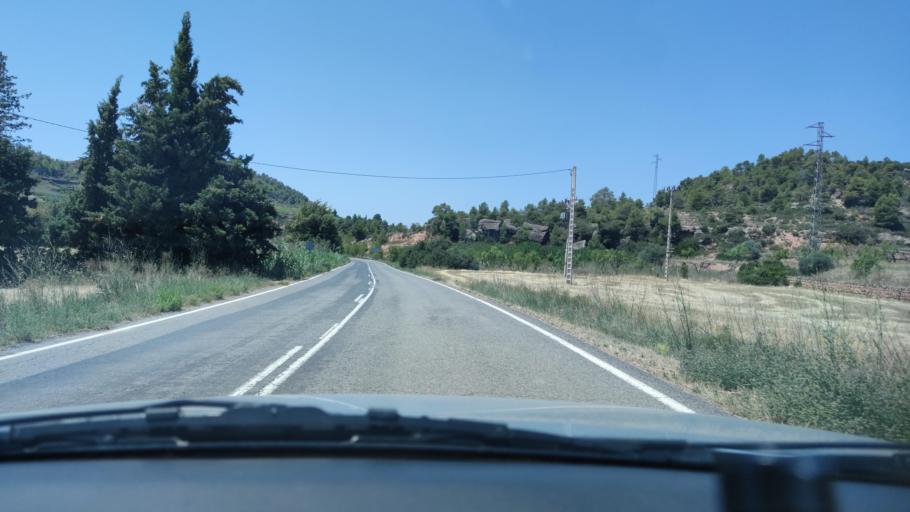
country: ES
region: Catalonia
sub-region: Provincia de Lleida
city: Juncosa
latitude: 41.3921
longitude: 0.7342
